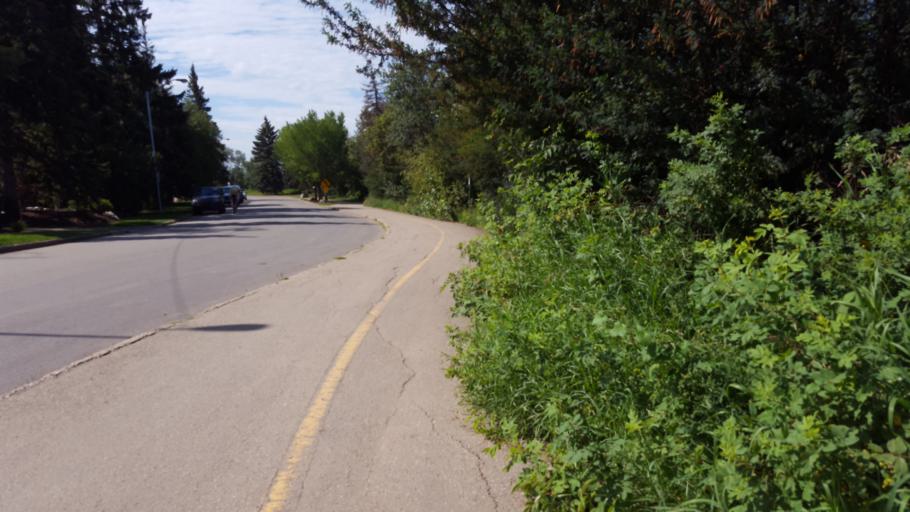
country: CA
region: Alberta
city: Edmonton
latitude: 53.5120
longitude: -113.5392
